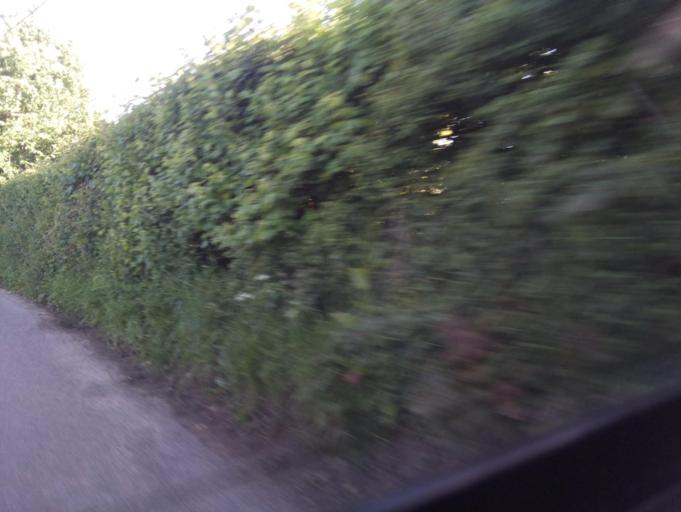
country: GB
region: England
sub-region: Devon
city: Topsham
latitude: 50.7076
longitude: -3.3827
